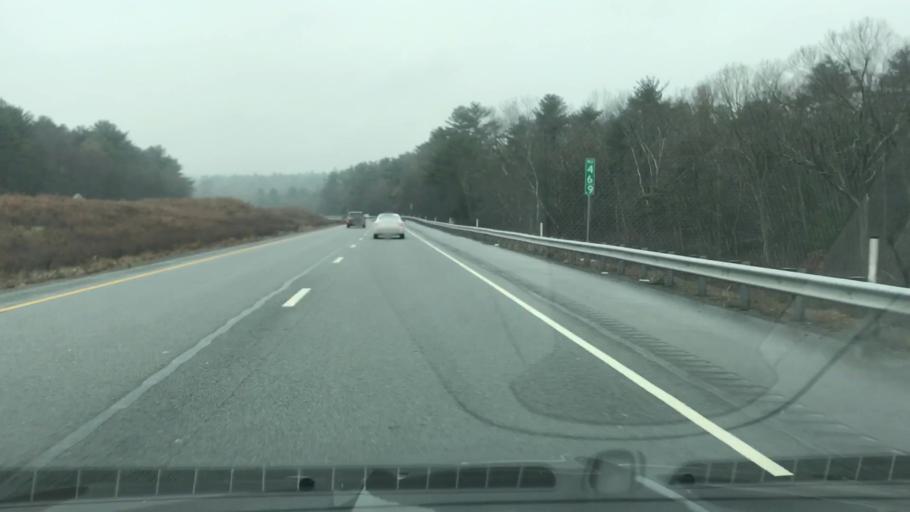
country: US
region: Pennsylvania
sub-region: Pike County
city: Milford
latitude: 41.3406
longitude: -74.8259
